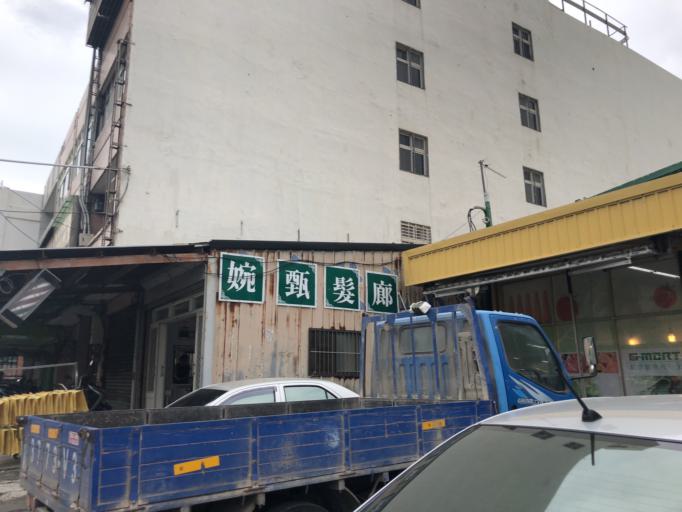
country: TW
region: Taiwan
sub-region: Chiayi
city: Taibao
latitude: 23.6992
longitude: 120.2021
